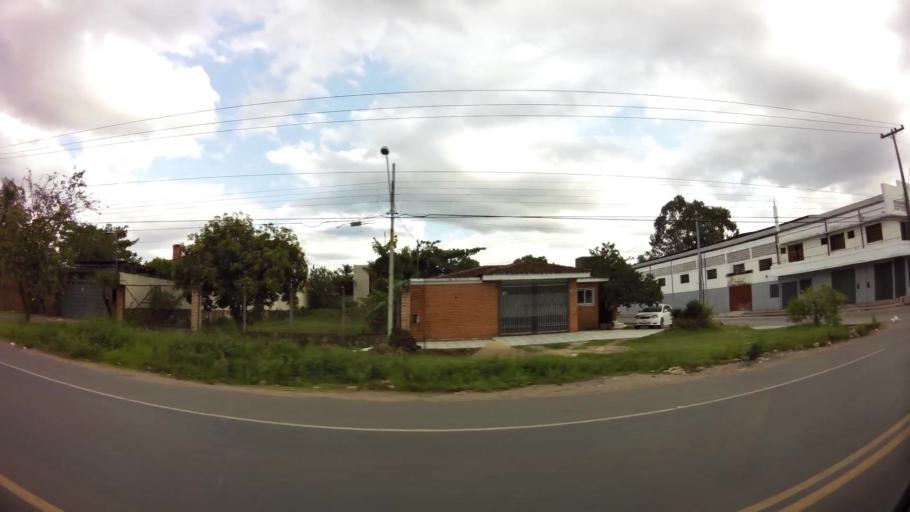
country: PY
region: Central
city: Fernando de la Mora
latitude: -25.2810
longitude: -57.5364
